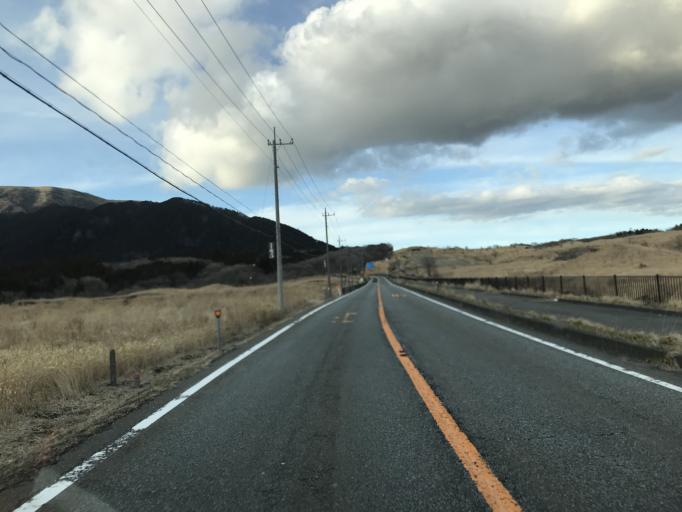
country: JP
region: Yamanashi
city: Fujikawaguchiko
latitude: 35.4211
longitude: 138.5916
